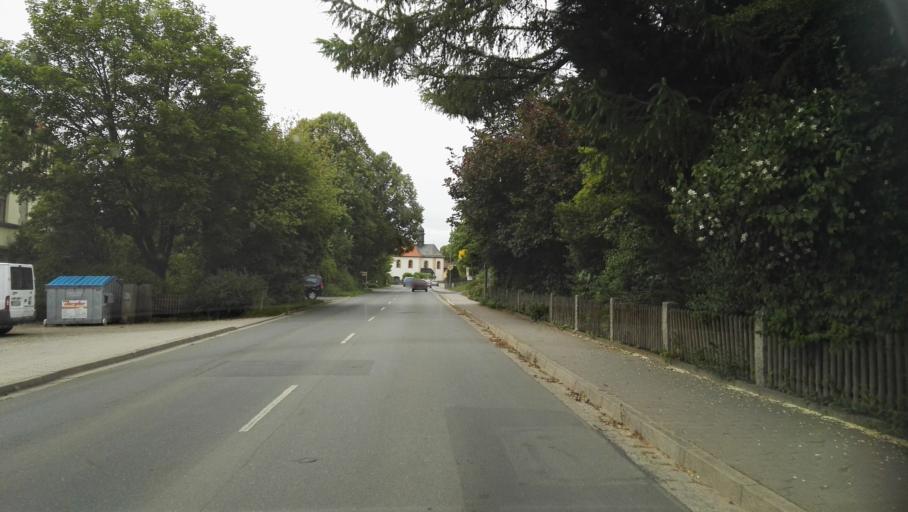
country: DE
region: Bavaria
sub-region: Upper Franconia
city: Hollfeld
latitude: 49.9326
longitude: 11.2961
